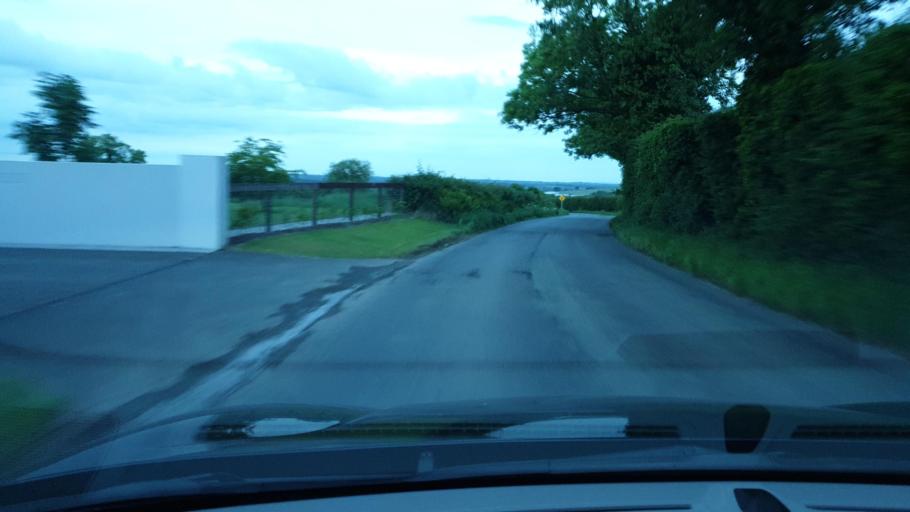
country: IE
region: Leinster
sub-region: An Mhi
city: Ashbourne
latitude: 53.5702
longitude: -6.3942
